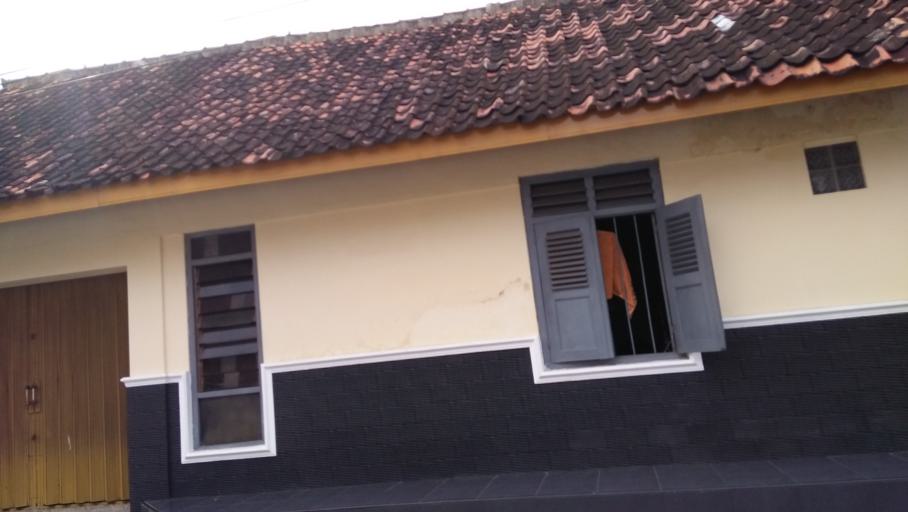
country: ID
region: Daerah Istimewa Yogyakarta
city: Yogyakarta
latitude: -7.7661
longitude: 110.3865
